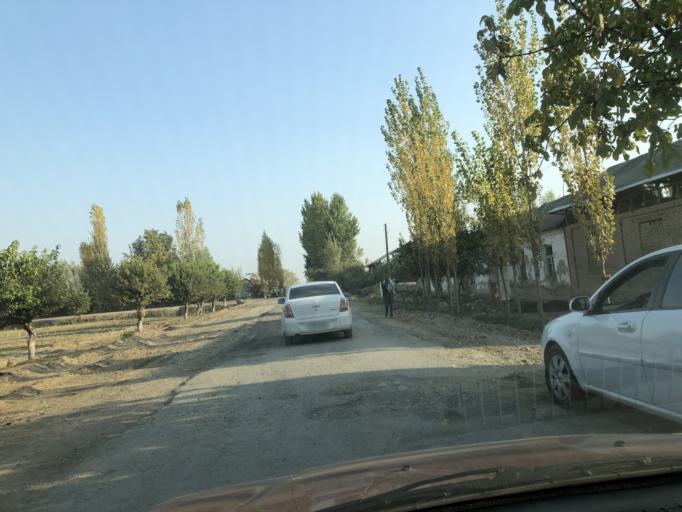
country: UZ
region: Namangan
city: Uychi
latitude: 41.0647
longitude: 71.9871
